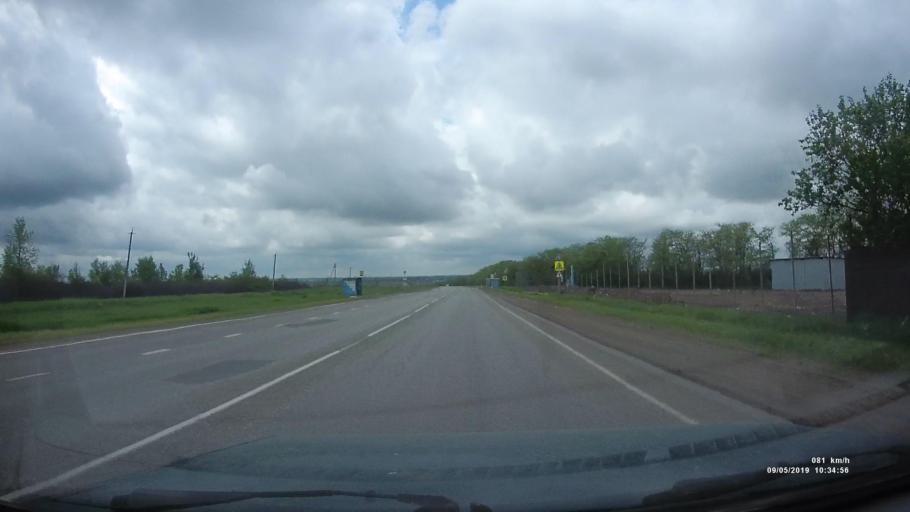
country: RU
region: Rostov
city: Peshkovo
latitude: 47.0486
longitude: 39.4163
